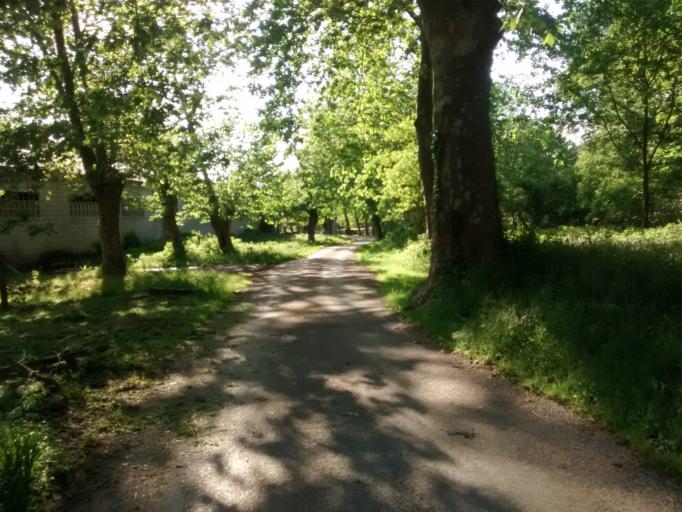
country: ES
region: Cantabria
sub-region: Provincia de Cantabria
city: Entrambasaguas
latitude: 43.3396
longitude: -3.6704
